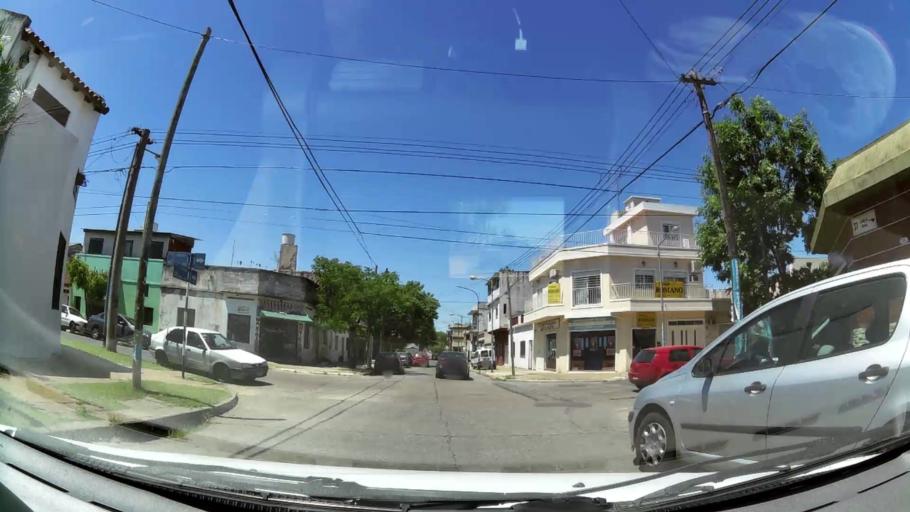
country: AR
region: Buenos Aires
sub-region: Partido de General San Martin
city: General San Martin
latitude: -34.5674
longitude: -58.5179
